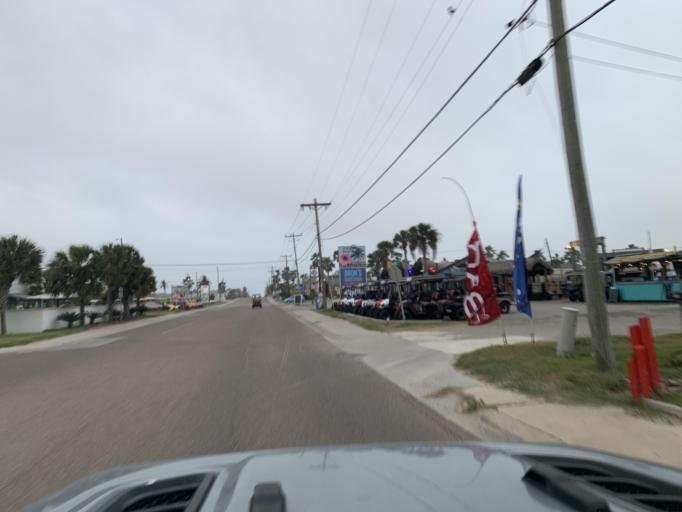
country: US
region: Texas
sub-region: Nueces County
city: Port Aransas
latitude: 27.8271
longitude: -97.0656
